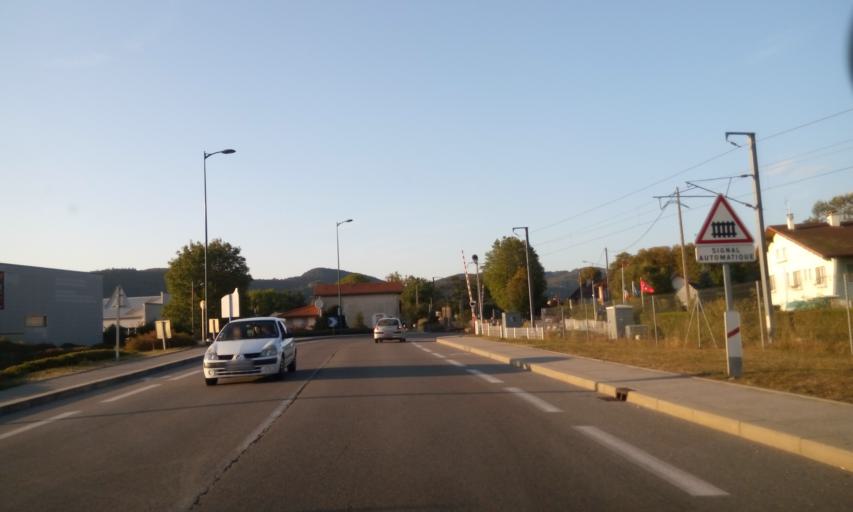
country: FR
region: Rhone-Alpes
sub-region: Departement de l'Ain
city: Montreal-la-Cluse
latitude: 46.1661
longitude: 5.5716
